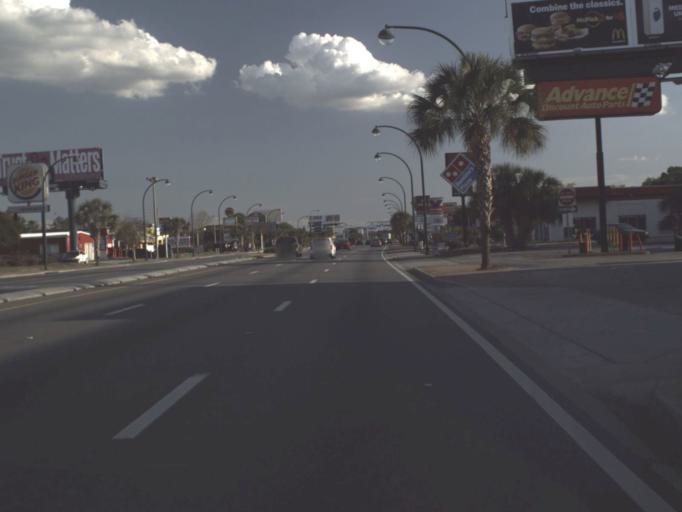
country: US
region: Florida
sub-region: Orange County
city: Sky Lake
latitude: 28.4714
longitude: -81.3968
